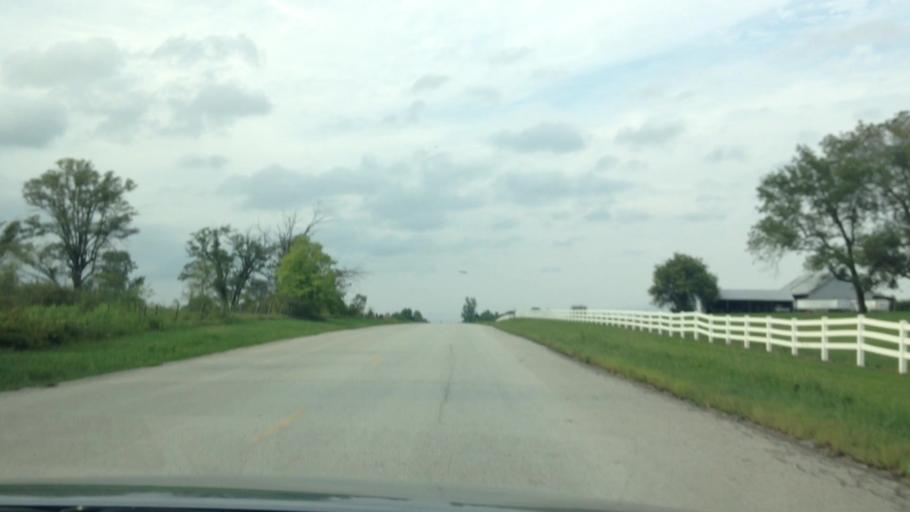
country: US
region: Missouri
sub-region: Clay County
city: Smithville
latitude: 39.3546
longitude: -94.6787
